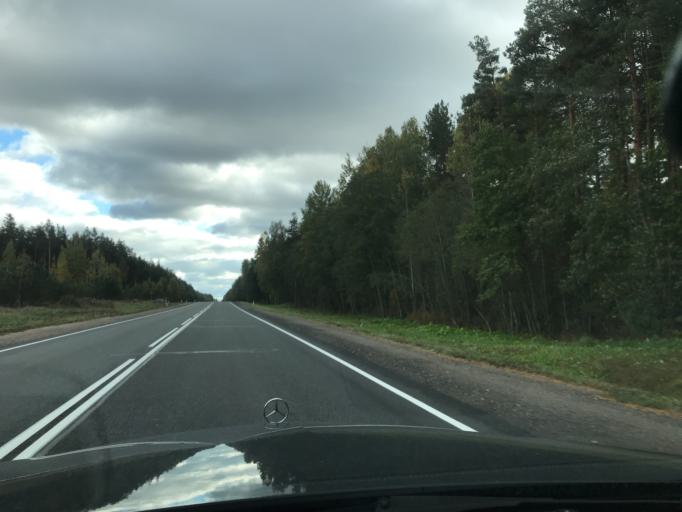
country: RU
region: Pskov
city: Opochka
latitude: 56.9752
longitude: 28.6286
